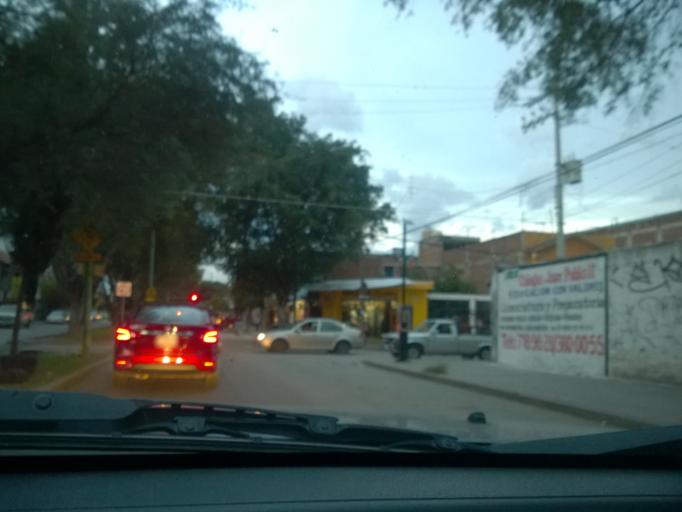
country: MX
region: Guanajuato
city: Leon
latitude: 21.1328
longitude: -101.6512
